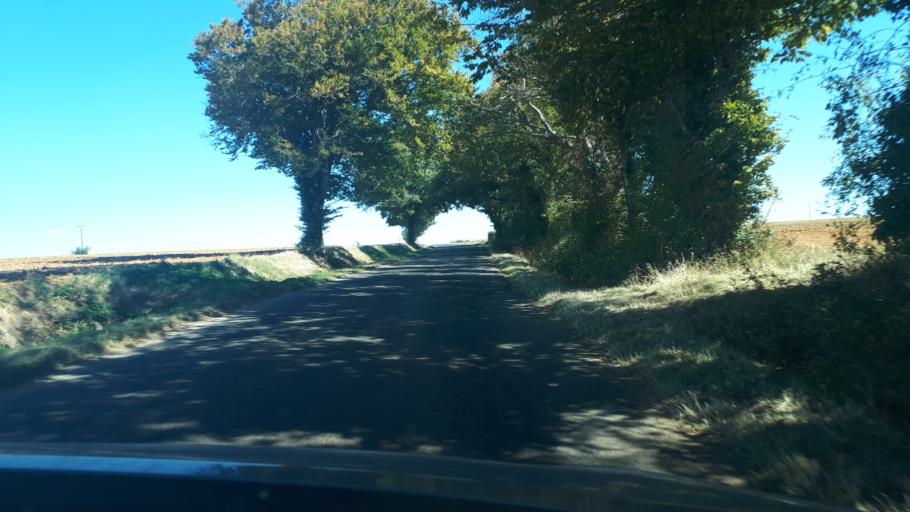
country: FR
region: Centre
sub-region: Departement du Cher
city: Sancerre
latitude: 47.3227
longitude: 2.7734
